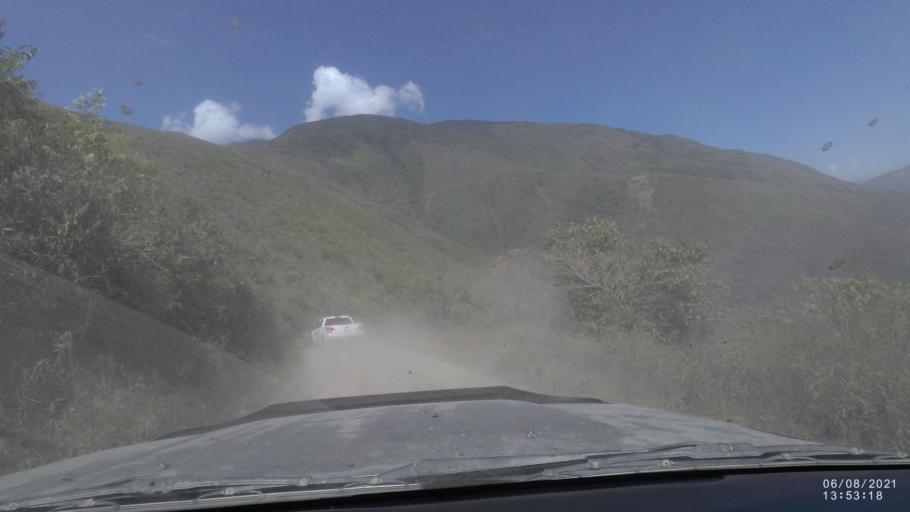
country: BO
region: La Paz
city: Quime
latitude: -16.6499
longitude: -66.7294
